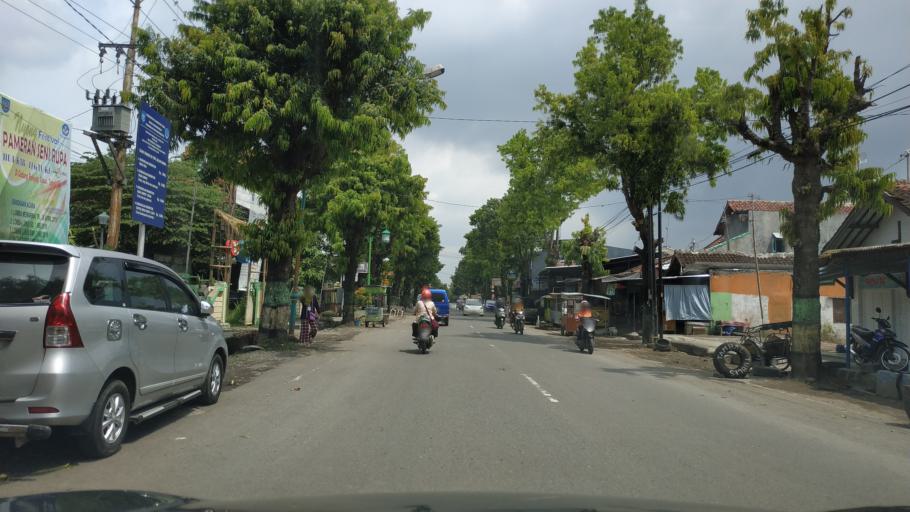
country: ID
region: Central Java
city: Slawi
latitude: -6.9924
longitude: 109.1406
